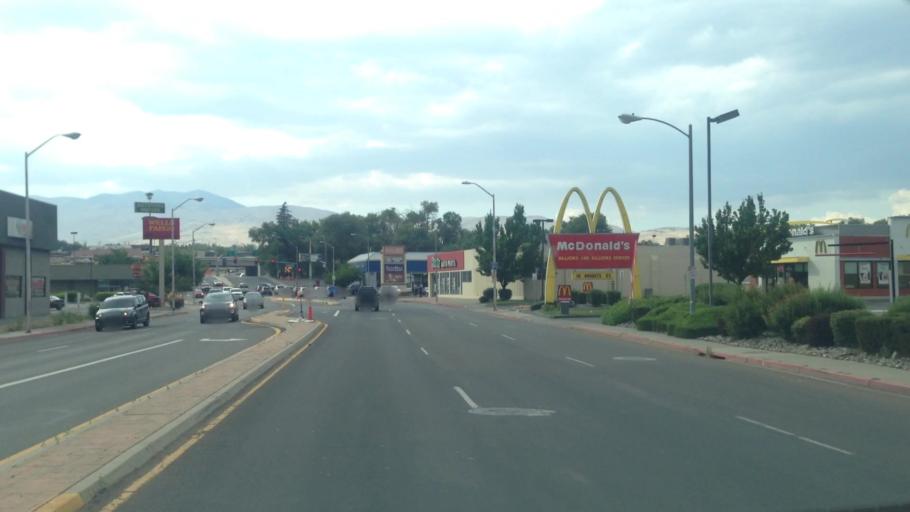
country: US
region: Nevada
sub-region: Washoe County
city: Reno
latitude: 39.5271
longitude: -119.8268
